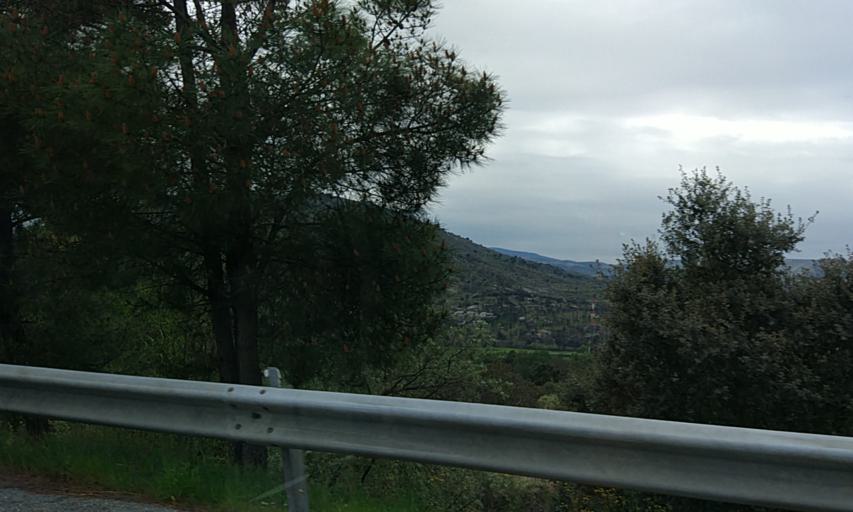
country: PT
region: Guarda
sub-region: Celorico da Beira
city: Celorico da Beira
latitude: 40.6255
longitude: -7.3068
